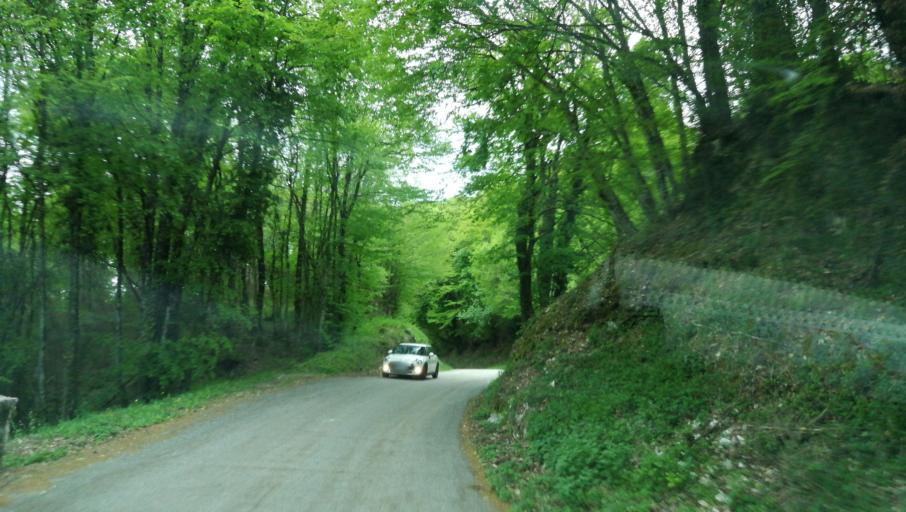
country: FR
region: Rhone-Alpes
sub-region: Departement de la Savoie
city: Chatillon
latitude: 45.7535
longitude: 5.8299
